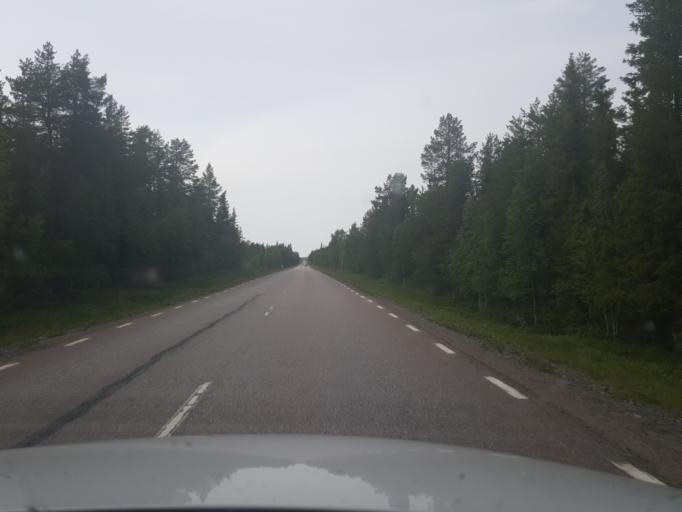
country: SE
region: Norrbotten
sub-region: Arjeplogs Kommun
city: Arjeplog
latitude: 65.7344
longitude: 18.0540
